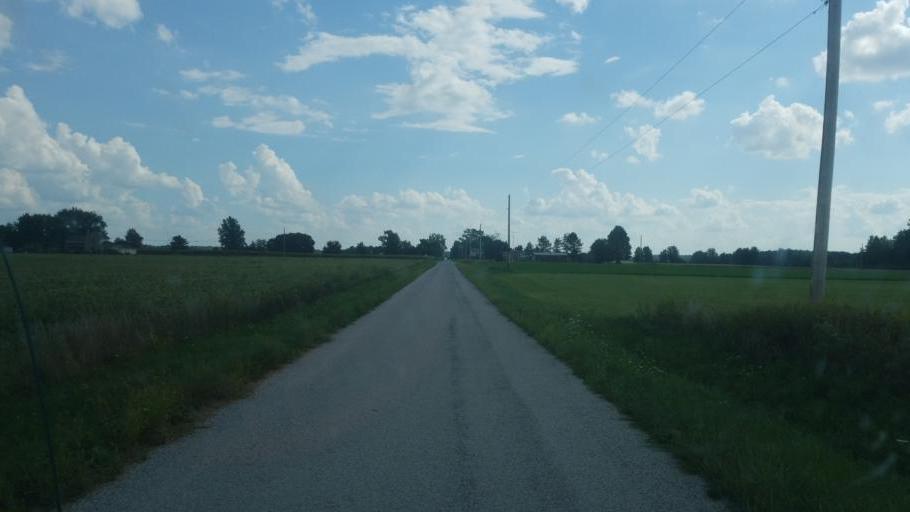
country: US
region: Ohio
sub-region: Huron County
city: Willard
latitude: 40.9841
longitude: -82.8160
